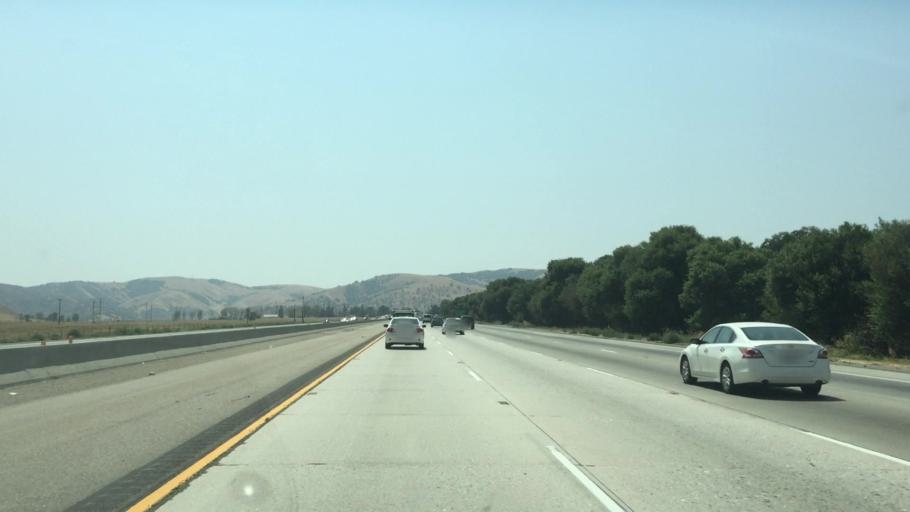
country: US
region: California
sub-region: Kern County
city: Lebec
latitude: 34.8495
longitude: -118.8709
